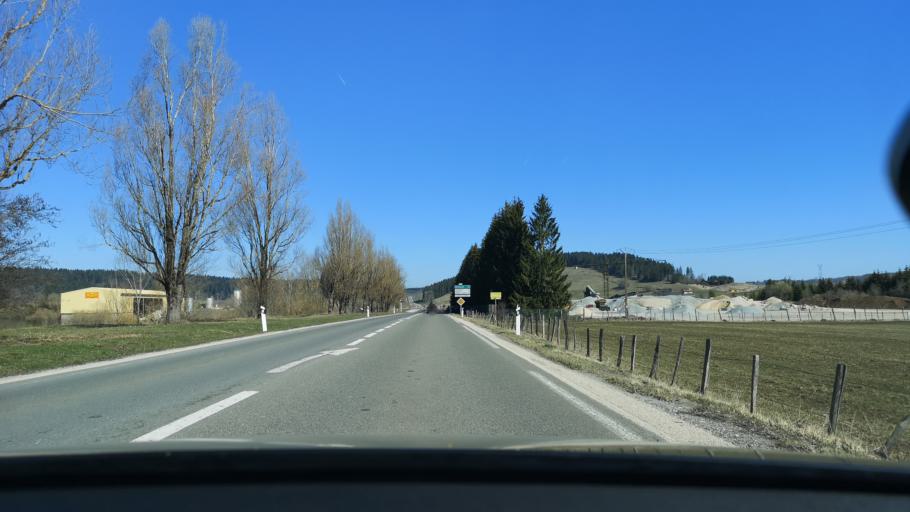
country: FR
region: Franche-Comte
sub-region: Departement du Doubs
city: Doubs
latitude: 46.9391
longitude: 6.3432
